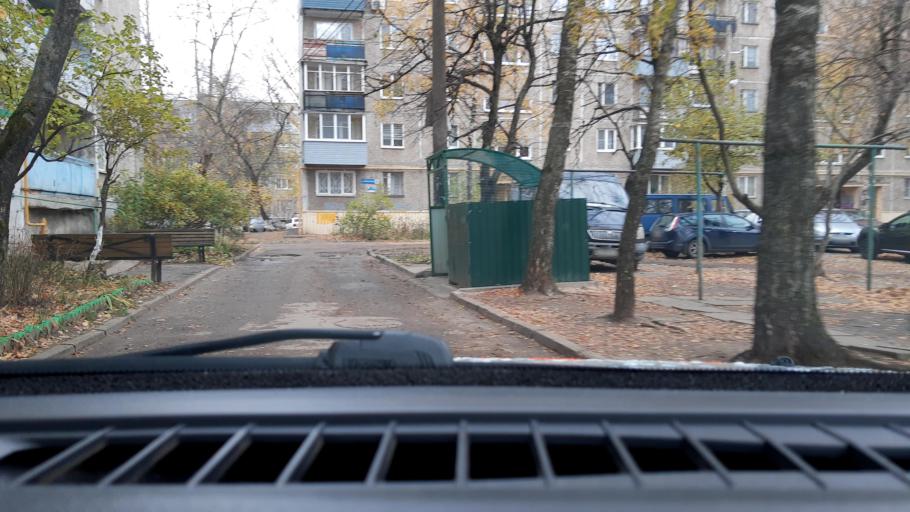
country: RU
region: Nizjnij Novgorod
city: Gorbatovka
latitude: 56.3613
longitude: 43.8173
